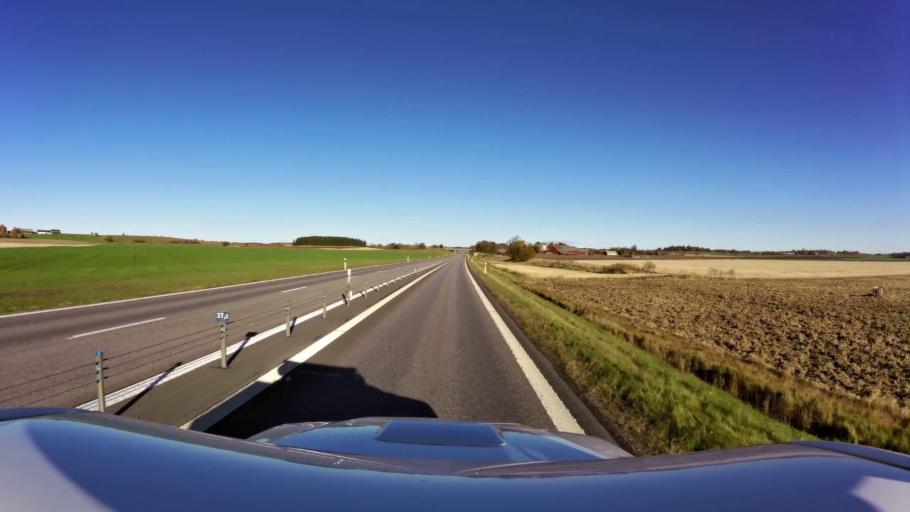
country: SE
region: OEstergoetland
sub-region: Linkopings Kommun
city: Berg
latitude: 58.4620
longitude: 15.4968
